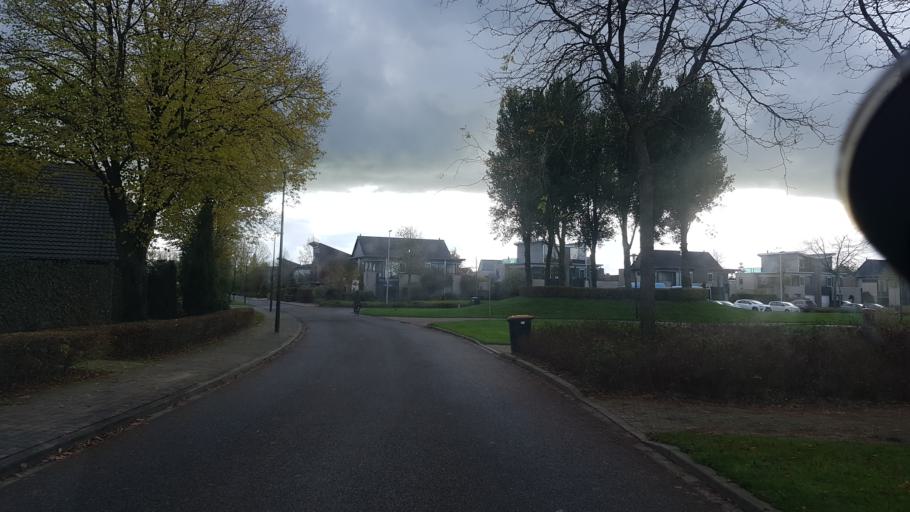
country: NL
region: Gelderland
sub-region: Gemeente Apeldoorn
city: Apeldoorn
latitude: 52.2173
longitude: 6.0161
